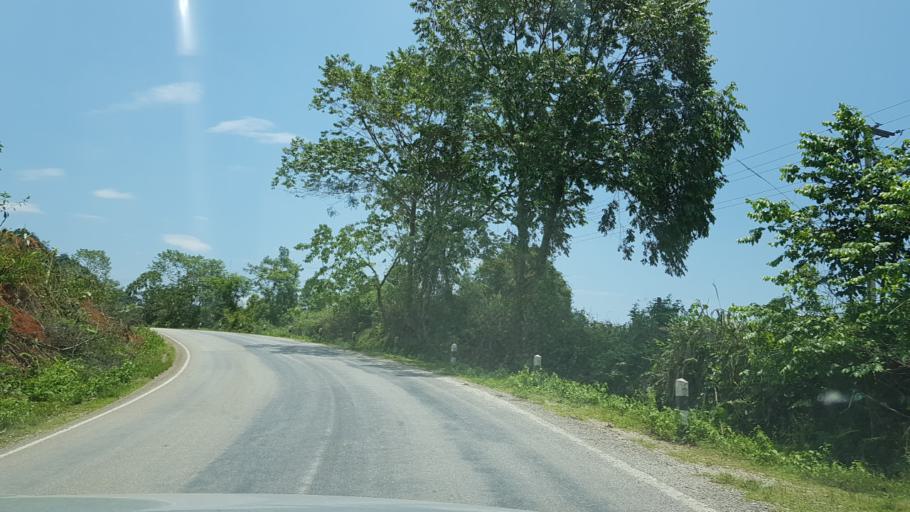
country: LA
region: Vientiane
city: Muang Kasi
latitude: 19.2709
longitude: 102.2148
